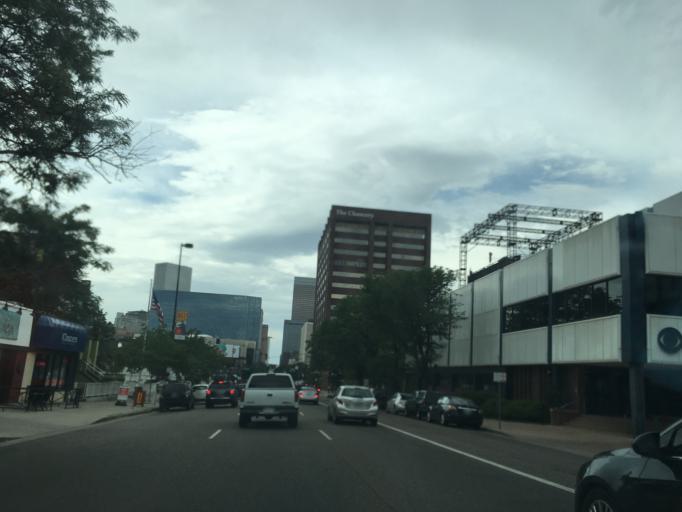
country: US
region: Colorado
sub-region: Denver County
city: Denver
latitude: 39.7324
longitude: -104.9862
